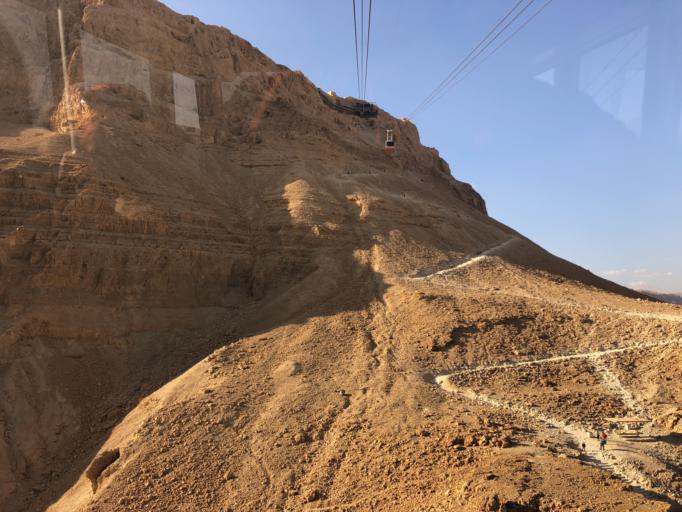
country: IL
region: Southern District
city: `En Boqeq
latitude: 31.3143
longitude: 35.3589
